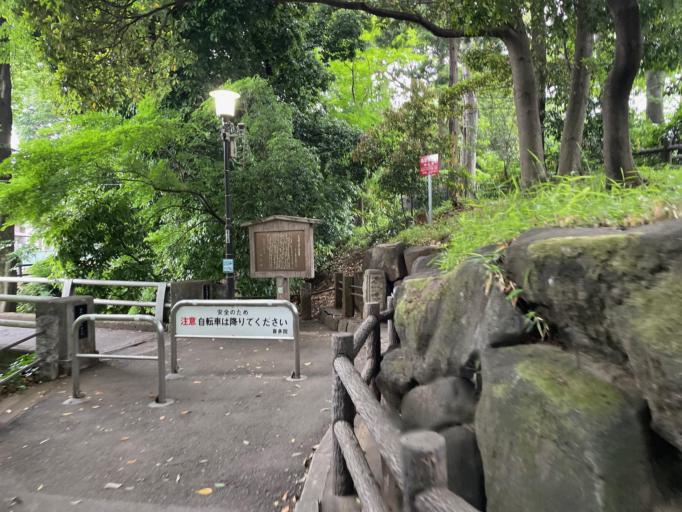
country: JP
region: Saitama
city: Kawagoe
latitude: 35.9171
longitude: 139.4888
